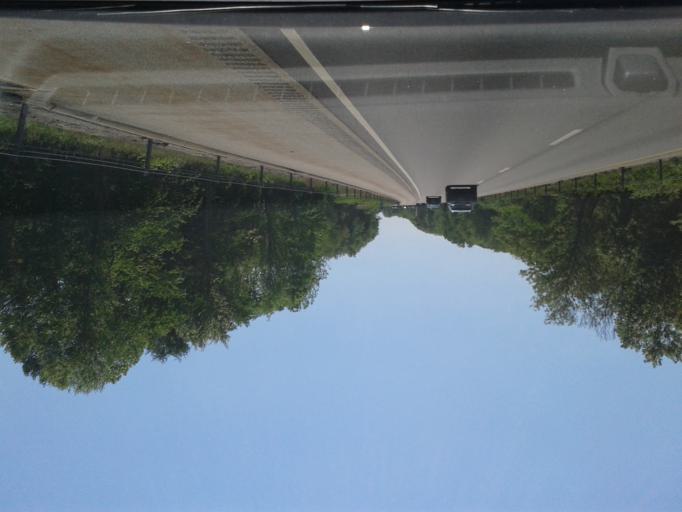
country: US
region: Connecticut
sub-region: New London County
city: Pawcatuck
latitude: 41.3916
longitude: -71.8758
